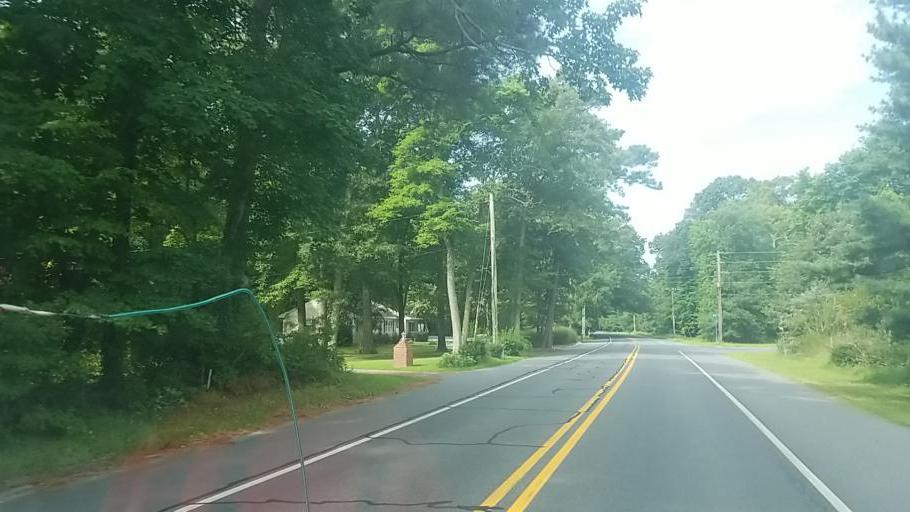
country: US
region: Delaware
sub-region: Sussex County
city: Long Neck
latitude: 38.5443
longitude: -75.1733
